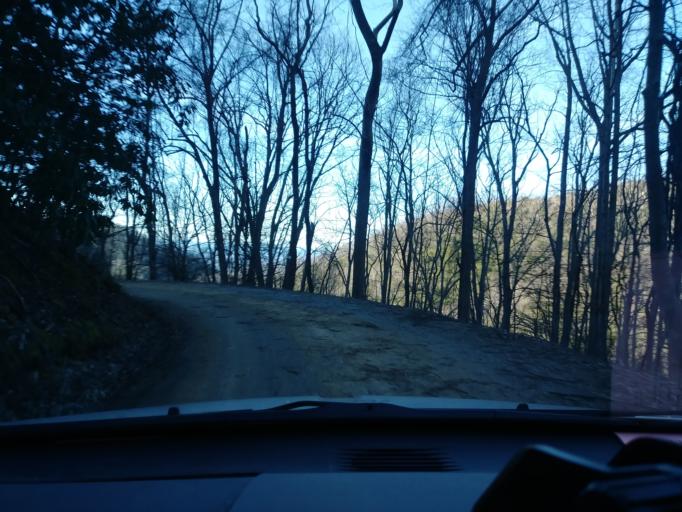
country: US
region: Tennessee
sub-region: Greene County
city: Tusculum
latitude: 36.0673
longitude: -82.6819
